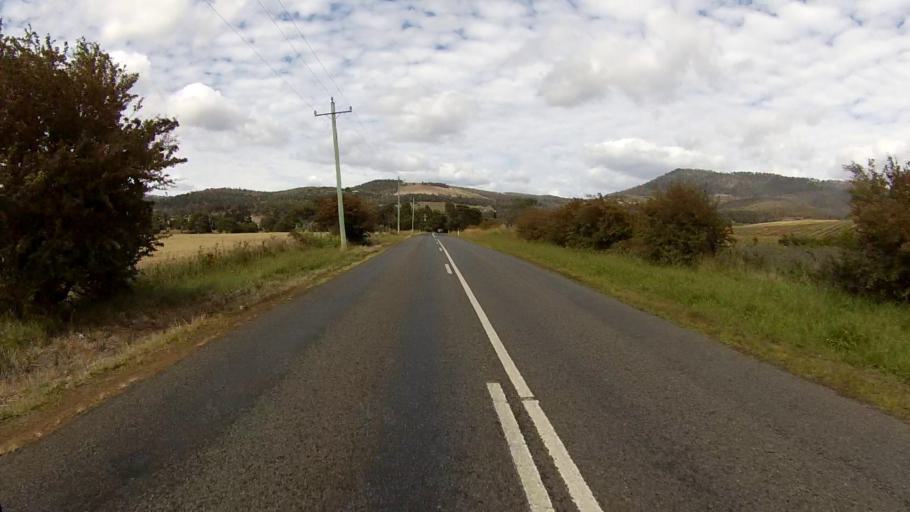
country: AU
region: Tasmania
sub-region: Clarence
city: Cambridge
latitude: -42.7567
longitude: 147.4050
